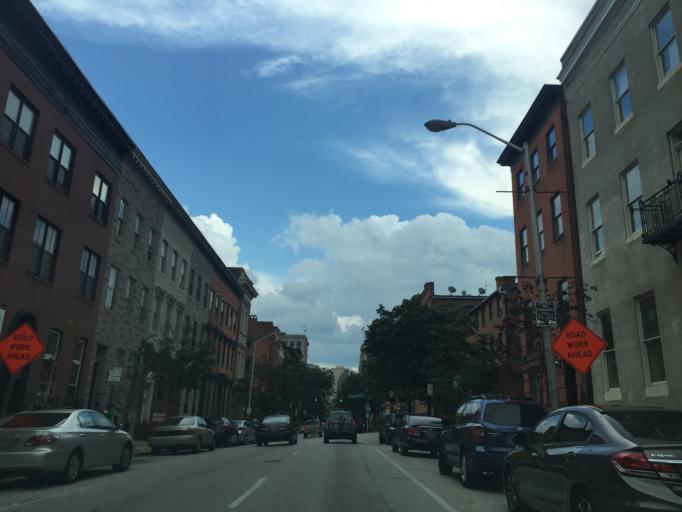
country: US
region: Maryland
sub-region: City of Baltimore
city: Baltimore
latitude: 39.2995
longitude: -76.6142
